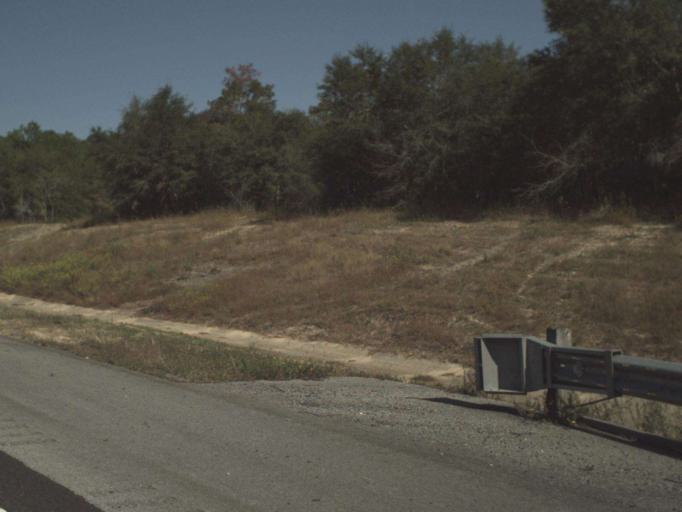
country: US
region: Florida
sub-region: Walton County
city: DeFuniak Springs
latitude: 30.7351
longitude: -86.2209
